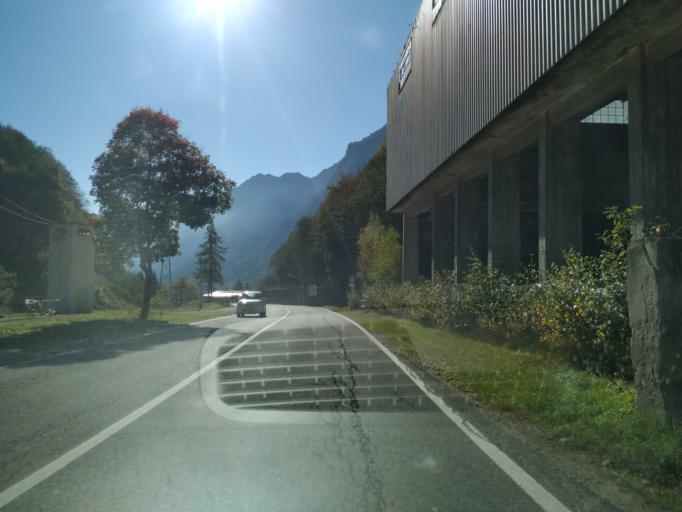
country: IT
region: Piedmont
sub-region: Provincia di Vercelli
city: Alagna Valsesia
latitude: 45.8451
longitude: 7.9396
